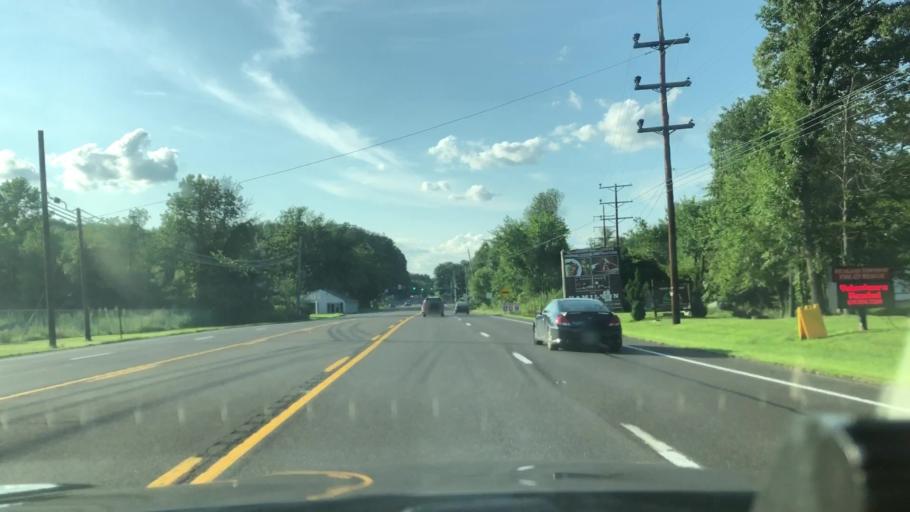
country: US
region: Pennsylvania
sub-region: Lehigh County
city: Coopersburg
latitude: 40.4788
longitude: -75.3736
